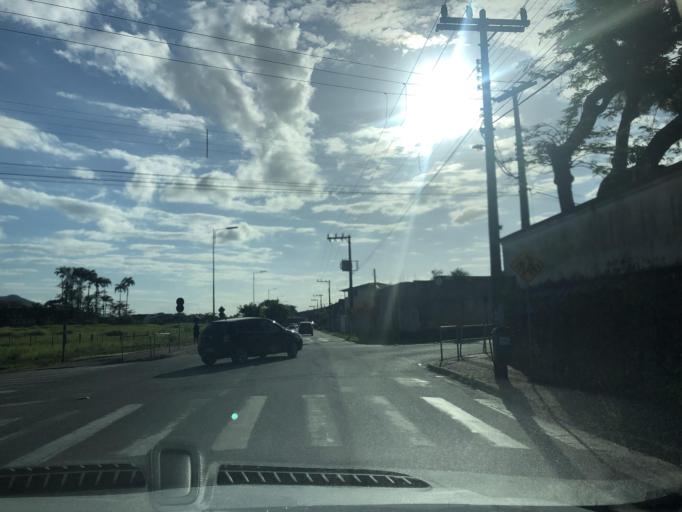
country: BR
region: Santa Catarina
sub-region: Sao Francisco Do Sul
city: Sao Francisco do Sul
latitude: -26.2489
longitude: -48.6387
